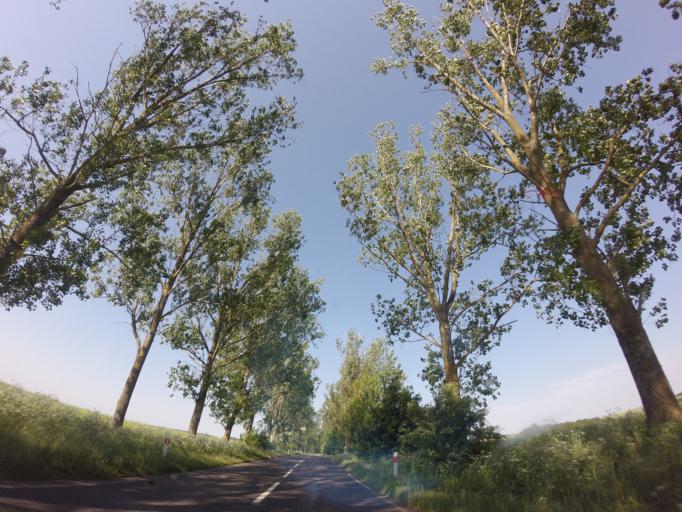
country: PL
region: West Pomeranian Voivodeship
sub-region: Powiat stargardzki
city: Kobylanka
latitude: 53.3173
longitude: 14.8479
